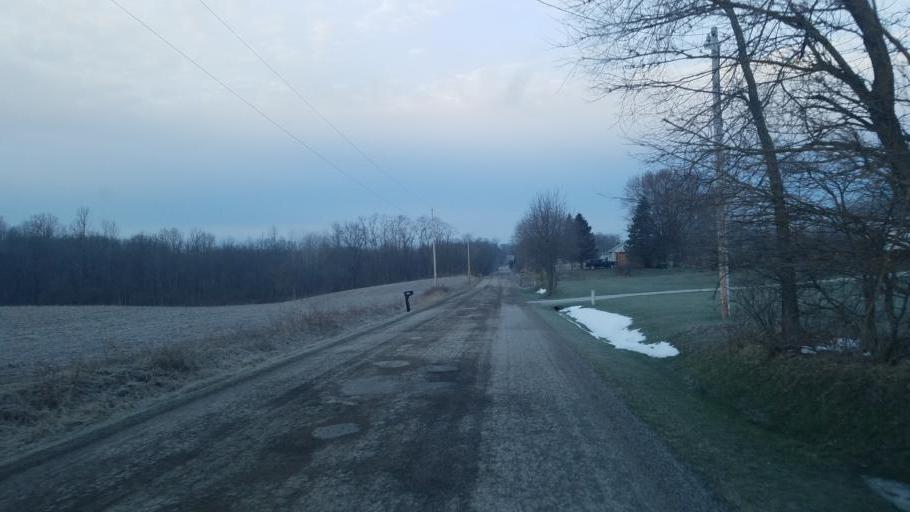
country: US
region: Ohio
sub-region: Morrow County
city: Mount Gilead
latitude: 40.4792
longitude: -82.7089
